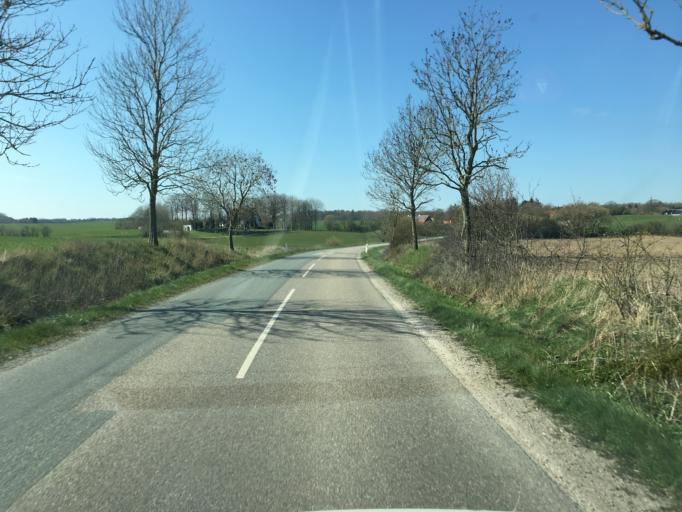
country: DK
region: South Denmark
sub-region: Sonderborg Kommune
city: Grasten
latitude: 54.9042
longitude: 9.5502
